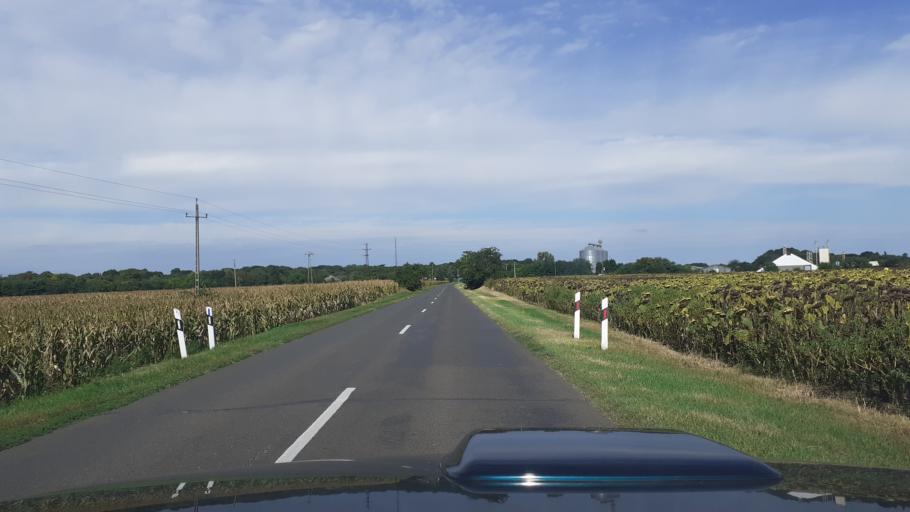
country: HU
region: Fejer
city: Pusztaszabolcs
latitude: 47.1279
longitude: 18.6801
